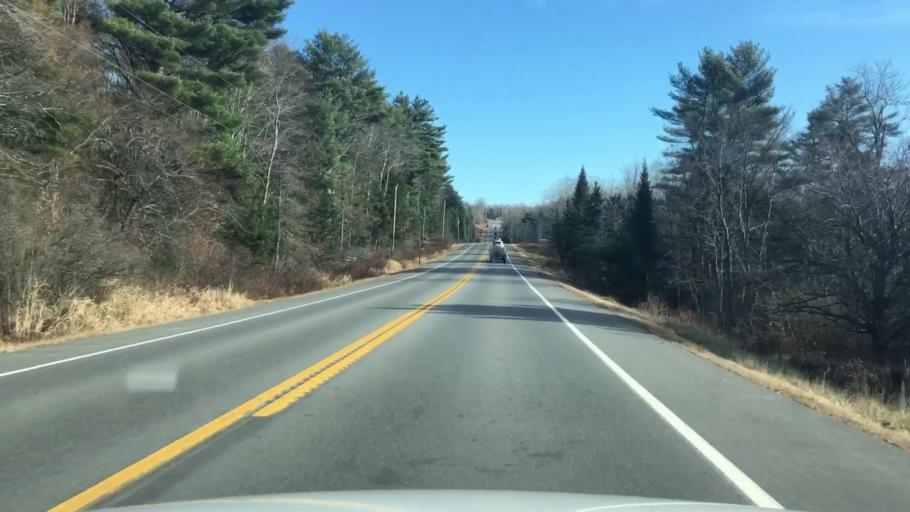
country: US
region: Maine
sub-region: Lincoln County
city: Jefferson
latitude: 44.2520
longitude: -69.4194
